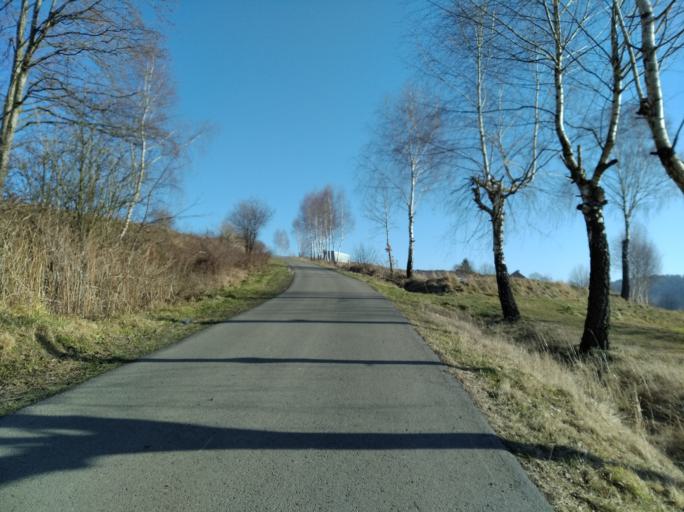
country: PL
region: Subcarpathian Voivodeship
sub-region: Powiat strzyzowski
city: Konieczkowa
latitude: 49.8585
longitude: 21.9444
